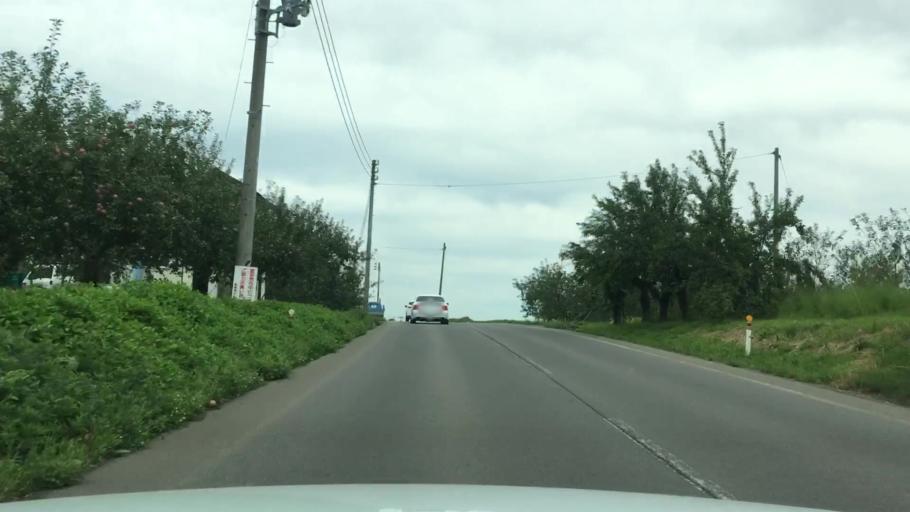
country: JP
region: Aomori
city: Hirosaki
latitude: 40.6566
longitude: 140.4202
